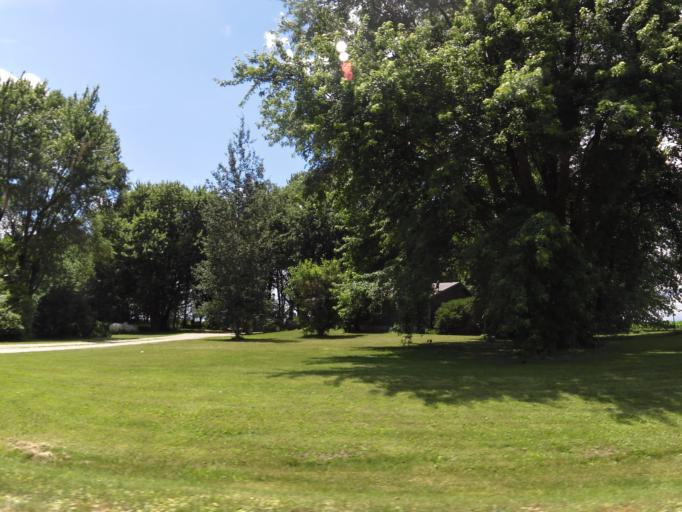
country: US
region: Iowa
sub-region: Buchanan County
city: Independence
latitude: 42.5305
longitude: -91.8900
